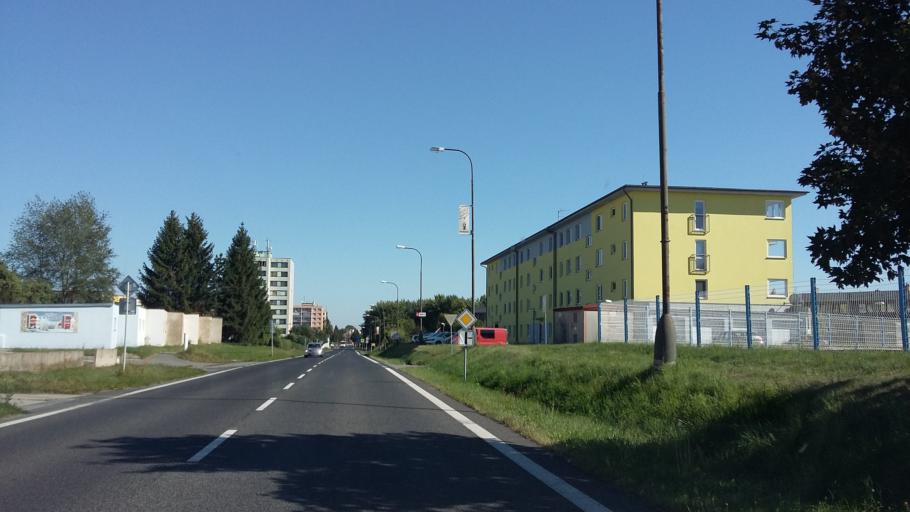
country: CZ
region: Central Bohemia
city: Bela pod Bezdezem
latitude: 50.5070
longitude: 14.7910
